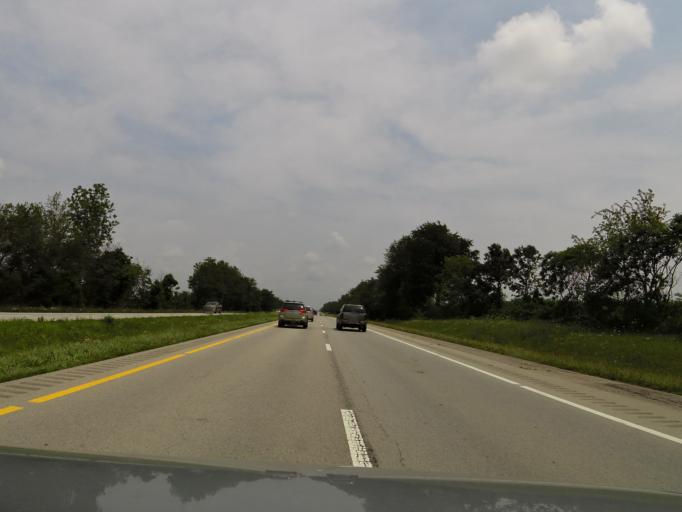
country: US
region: Kentucky
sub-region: Hardin County
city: Elizabethtown
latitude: 37.6230
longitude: -85.9487
